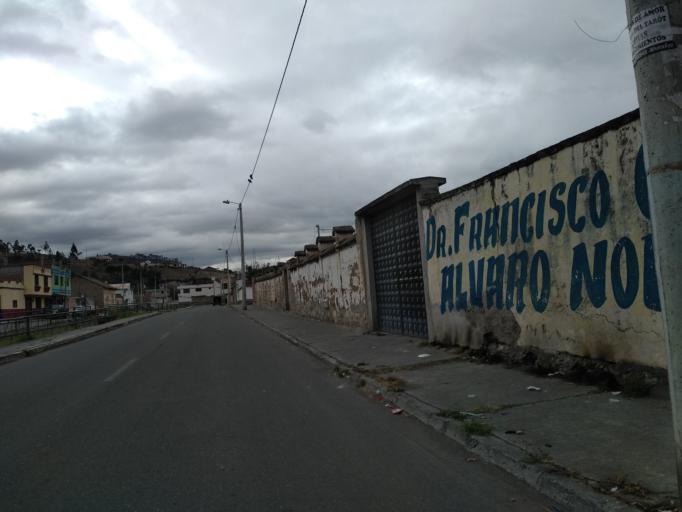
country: EC
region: Chimborazo
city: Riobamba
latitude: -1.6883
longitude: -78.6769
